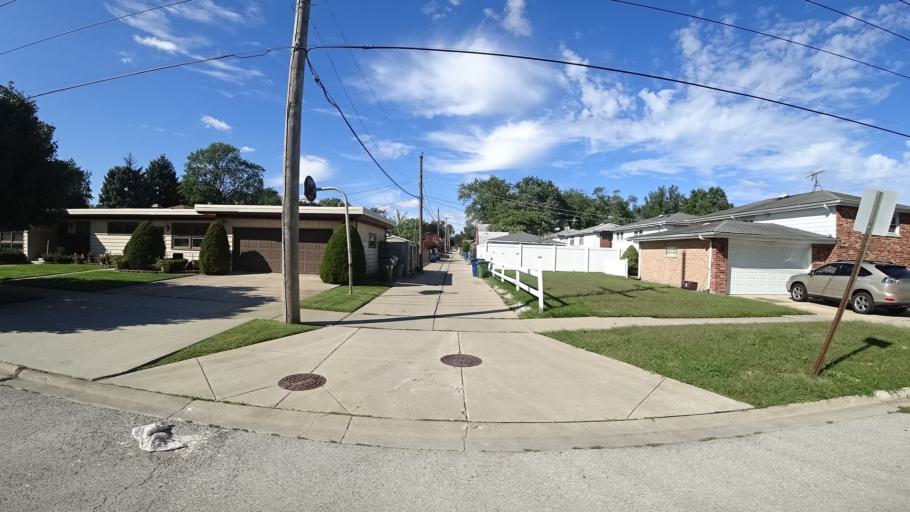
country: US
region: Illinois
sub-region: Cook County
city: Oak Lawn
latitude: 41.7125
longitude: -87.7557
